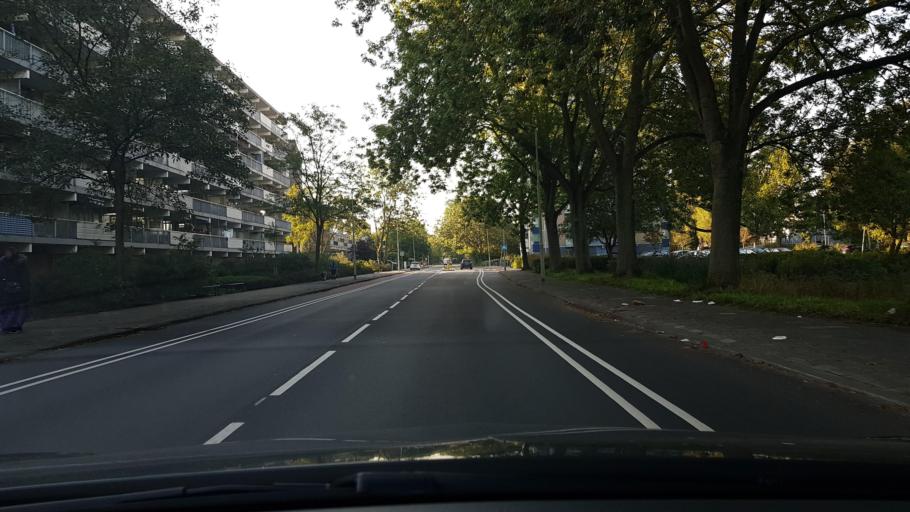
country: NL
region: North Holland
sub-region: Gemeente Haarlem
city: Haarlem
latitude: 52.3569
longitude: 4.6572
